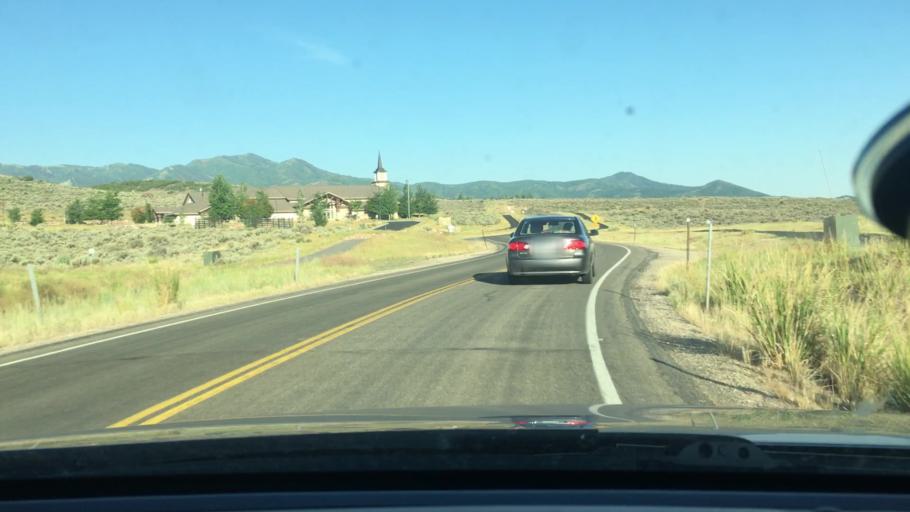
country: US
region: Utah
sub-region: Summit County
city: Snyderville
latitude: 40.7120
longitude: -111.4975
